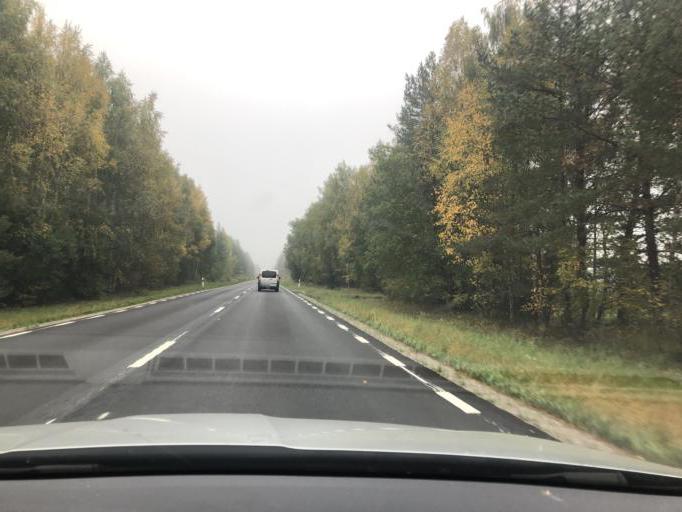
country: SE
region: Uppsala
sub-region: Tierps Kommun
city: Orbyhus
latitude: 60.2507
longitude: 17.6453
